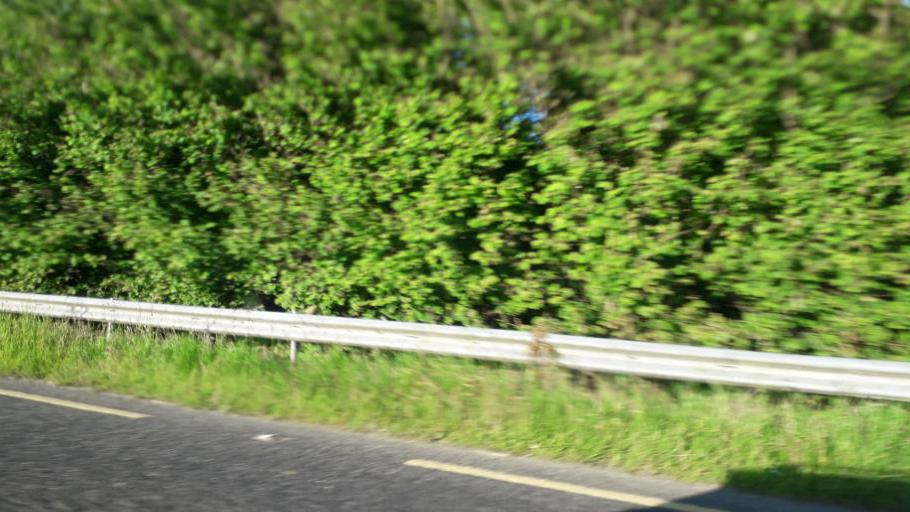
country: IE
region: Leinster
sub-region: Loch Garman
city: Loch Garman
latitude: 52.3411
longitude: -6.5156
